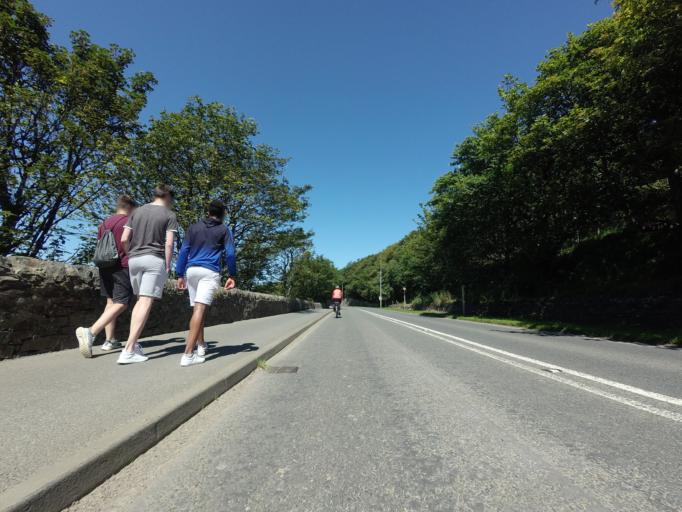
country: GB
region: Scotland
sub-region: Aberdeenshire
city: Macduff
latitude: 57.6605
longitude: -2.5118
